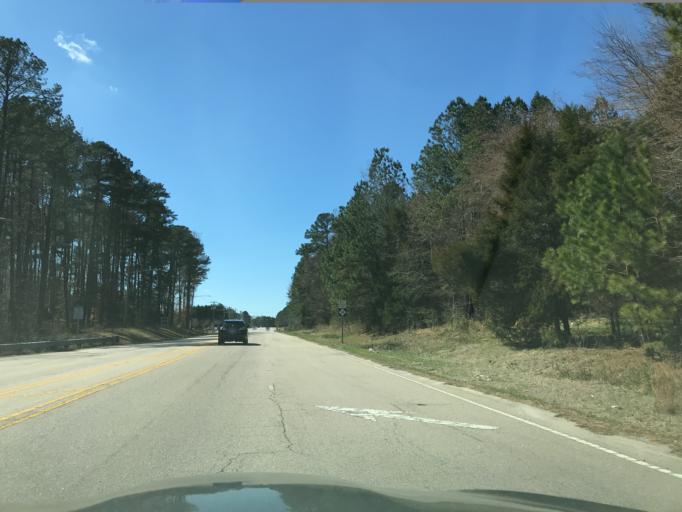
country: US
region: North Carolina
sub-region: Wake County
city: Wake Forest
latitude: 35.9776
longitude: -78.5443
